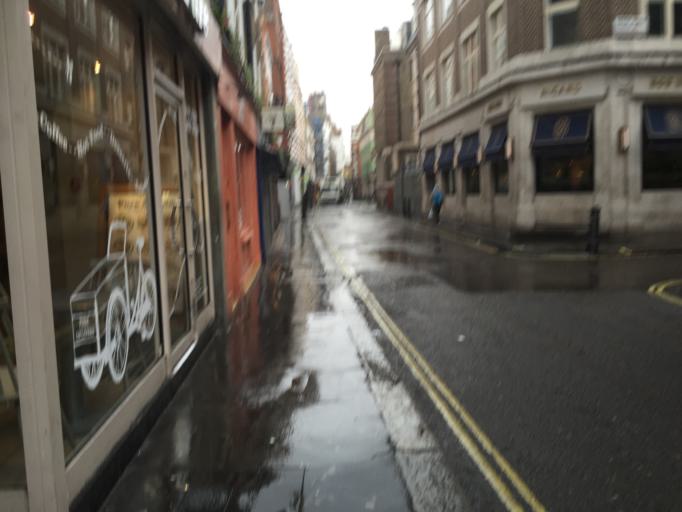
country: GB
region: England
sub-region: Greater London
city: London
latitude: 51.5124
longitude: -0.1376
